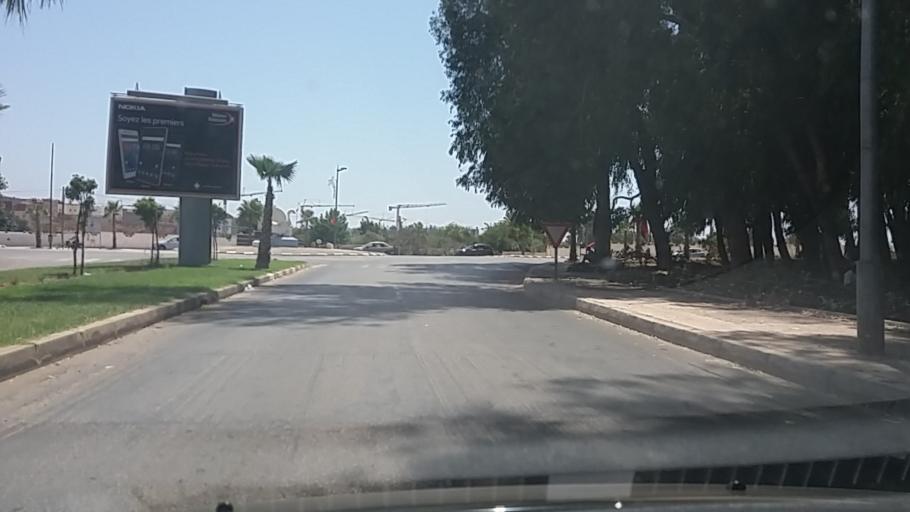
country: MA
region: Gharb-Chrarda-Beni Hssen
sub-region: Kenitra Province
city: Kenitra
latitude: 34.2491
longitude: -6.6151
